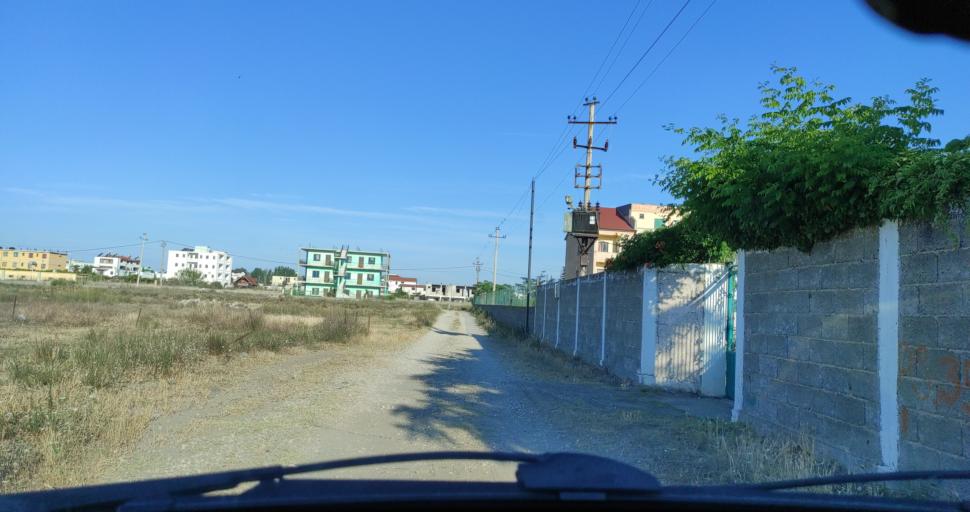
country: AL
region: Shkoder
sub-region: Rrethi i Shkodres
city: Velipoje
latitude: 41.8666
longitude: 19.4369
